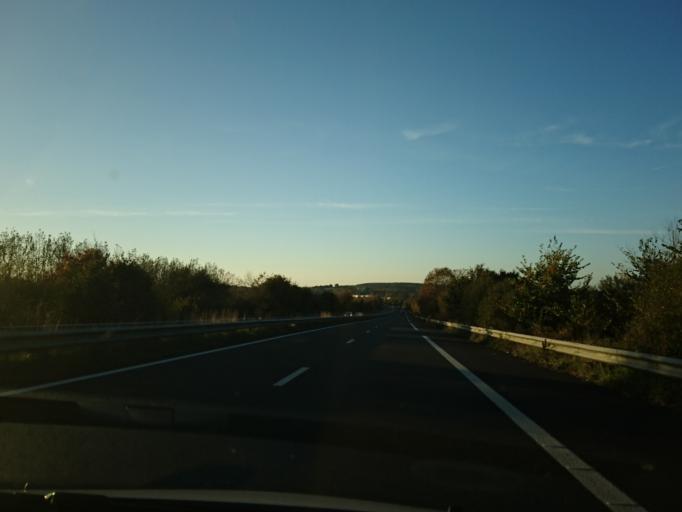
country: FR
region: Brittany
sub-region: Departement des Cotes-d'Armor
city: Plounevez-Moedec
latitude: 48.5526
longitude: -3.4700
